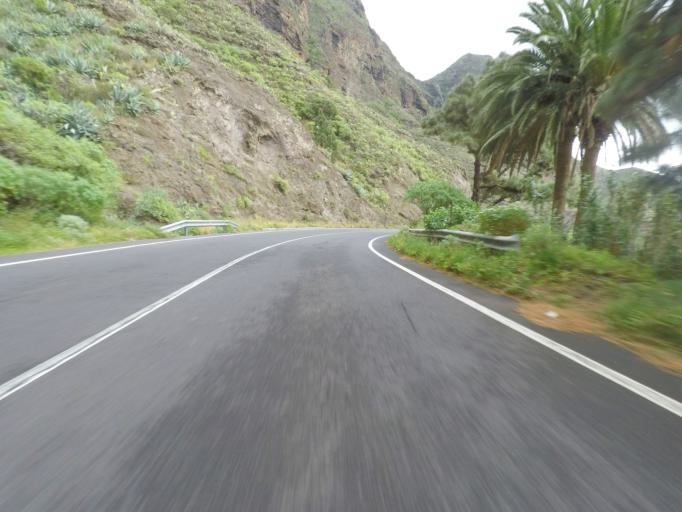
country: ES
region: Canary Islands
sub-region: Provincia de Santa Cruz de Tenerife
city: Hermigua
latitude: 28.1324
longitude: -17.1822
